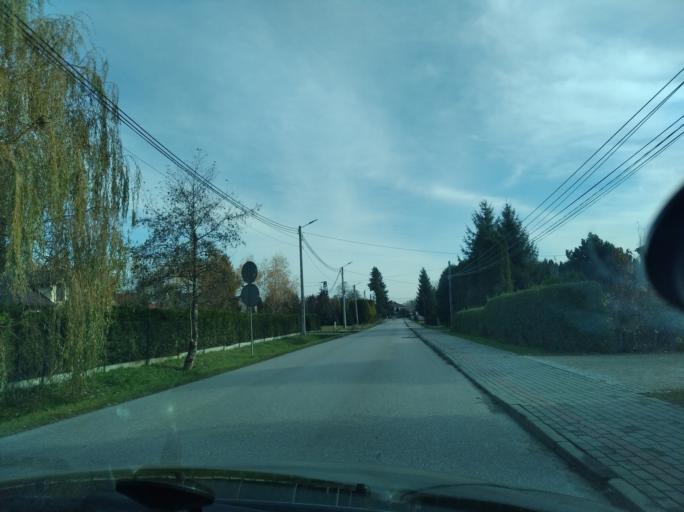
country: PL
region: Subcarpathian Voivodeship
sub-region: Powiat lancucki
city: Kraczkowa
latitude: 50.0381
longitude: 22.1634
